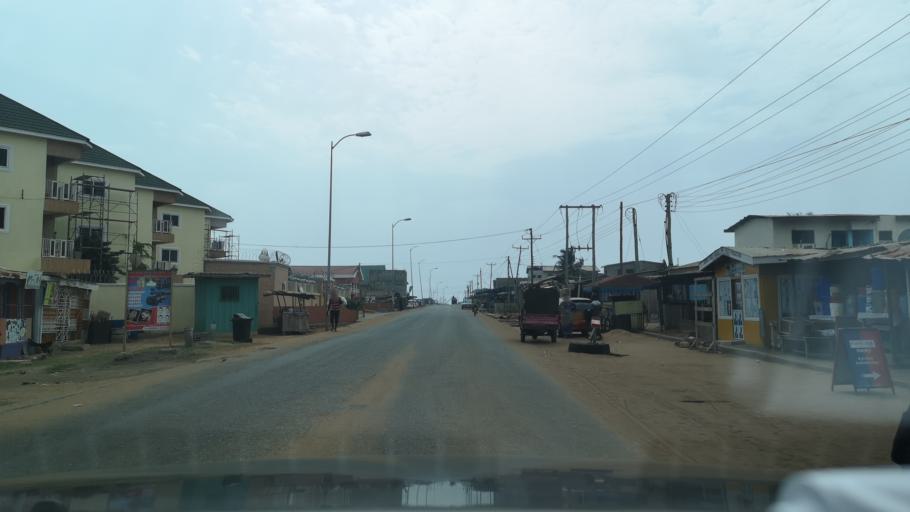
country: GH
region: Greater Accra
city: Nungua
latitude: 5.6141
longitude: -0.0501
